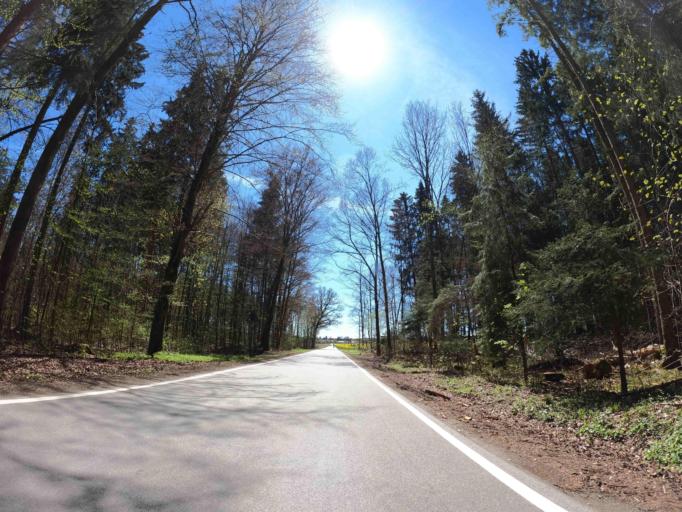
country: DE
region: Bavaria
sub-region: Upper Bavaria
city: Oberhaching
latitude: 48.0013
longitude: 11.5607
